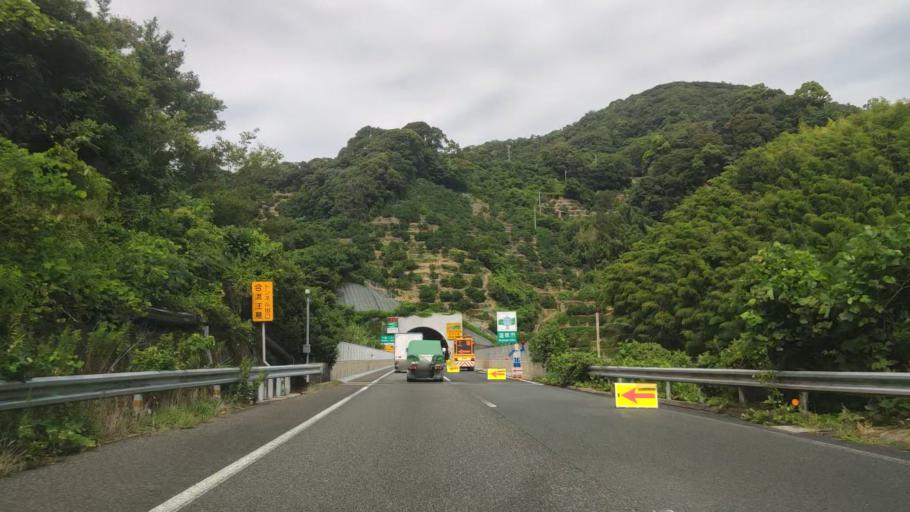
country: JP
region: Wakayama
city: Kainan
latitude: 34.1140
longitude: 135.2000
